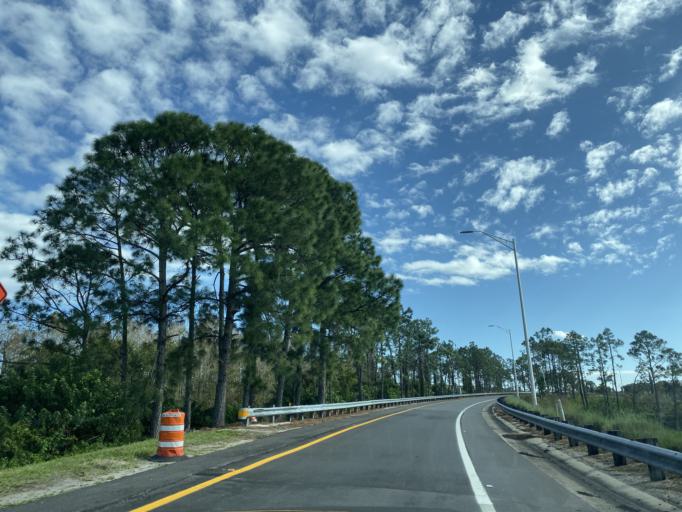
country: US
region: Florida
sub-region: Orange County
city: Conway
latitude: 28.4495
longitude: -81.2330
